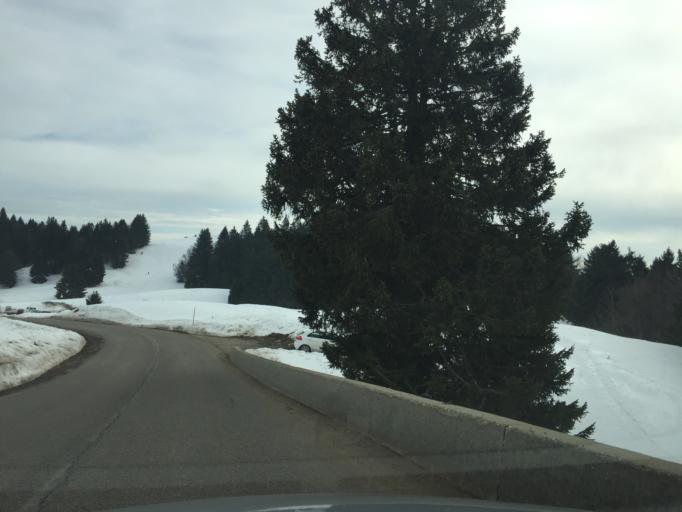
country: FR
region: Rhone-Alpes
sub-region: Departement de la Savoie
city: Mouxy
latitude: 45.6717
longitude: 5.9726
